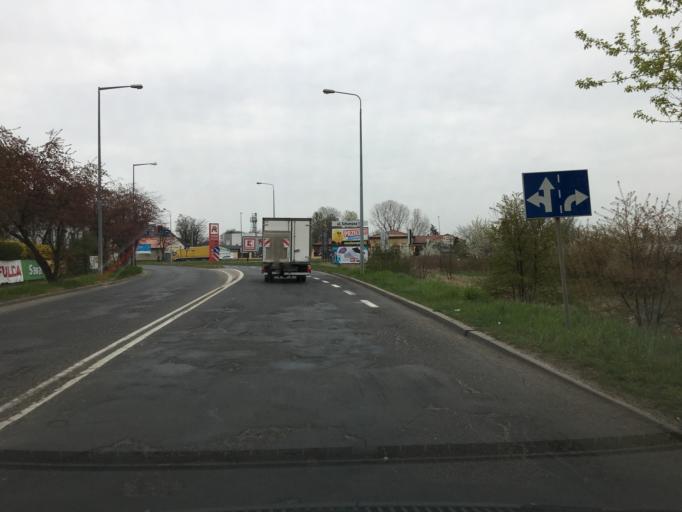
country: PL
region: Lower Silesian Voivodeship
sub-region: Legnica
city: Legnica
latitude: 51.1891
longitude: 16.1739
